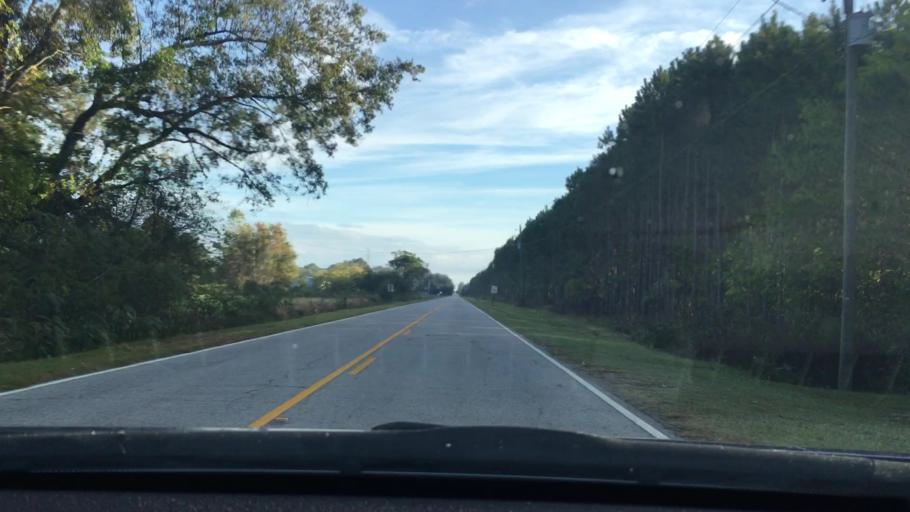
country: US
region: South Carolina
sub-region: Lee County
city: Bishopville
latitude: 34.1056
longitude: -80.1621
